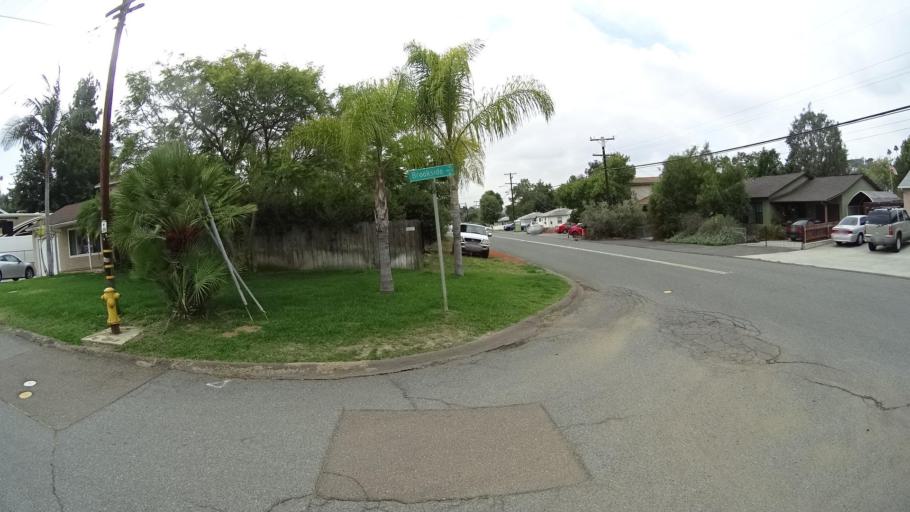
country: US
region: California
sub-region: San Diego County
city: Spring Valley
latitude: 32.7535
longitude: -116.9992
